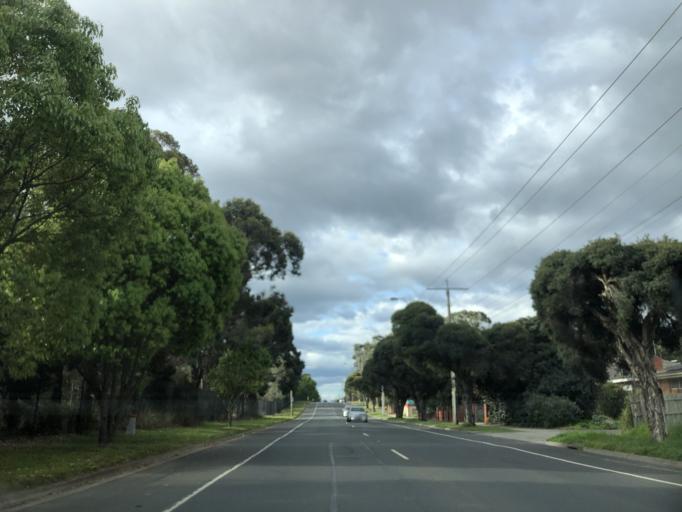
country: AU
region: Victoria
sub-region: Monash
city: Oakleigh South
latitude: -37.9224
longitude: 145.1014
